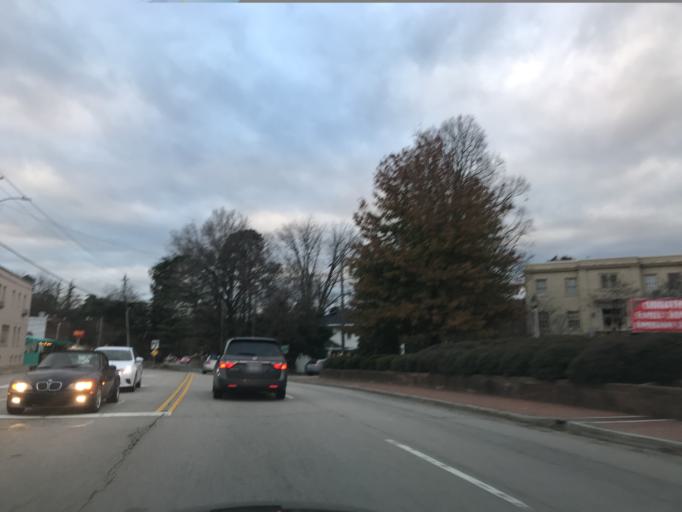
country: US
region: North Carolina
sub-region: Wake County
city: West Raleigh
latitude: 35.8042
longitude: -78.6459
